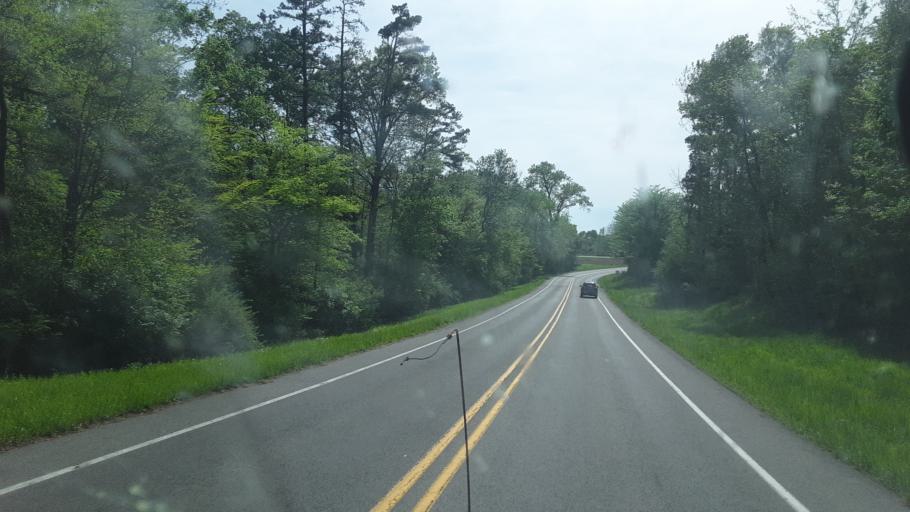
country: US
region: Illinois
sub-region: Jackson County
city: Carbondale
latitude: 37.6871
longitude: -89.2511
